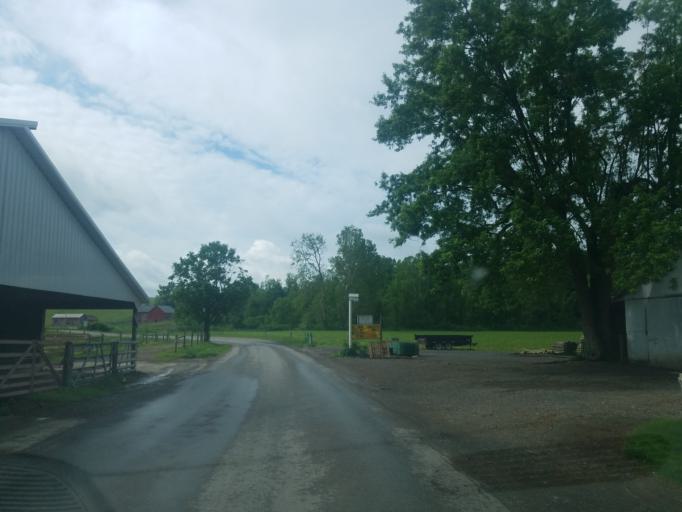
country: US
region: Ohio
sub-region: Holmes County
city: Millersburg
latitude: 40.4722
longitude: -81.8439
